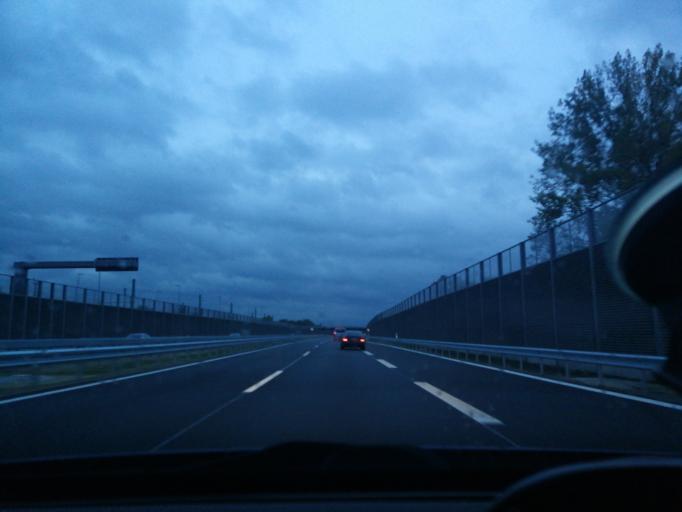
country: DE
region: Hamburg
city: Kleiner Grasbrook
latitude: 53.5022
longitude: 10.0059
